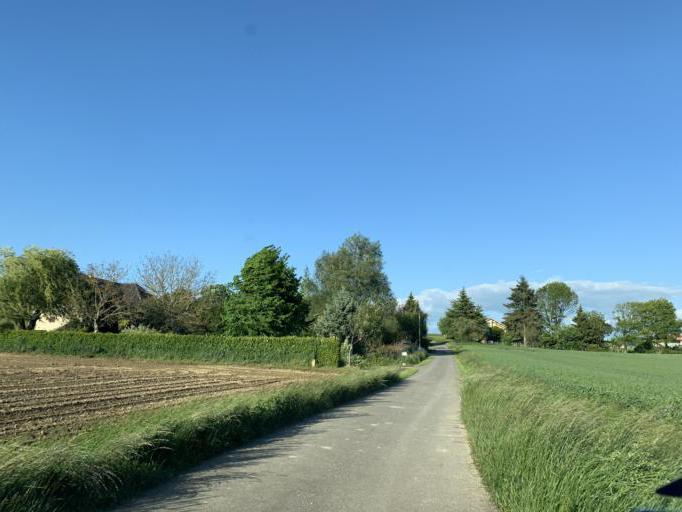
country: FR
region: Rhone-Alpes
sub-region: Departement de l'Ain
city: Perouges
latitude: 45.9054
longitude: 5.1379
